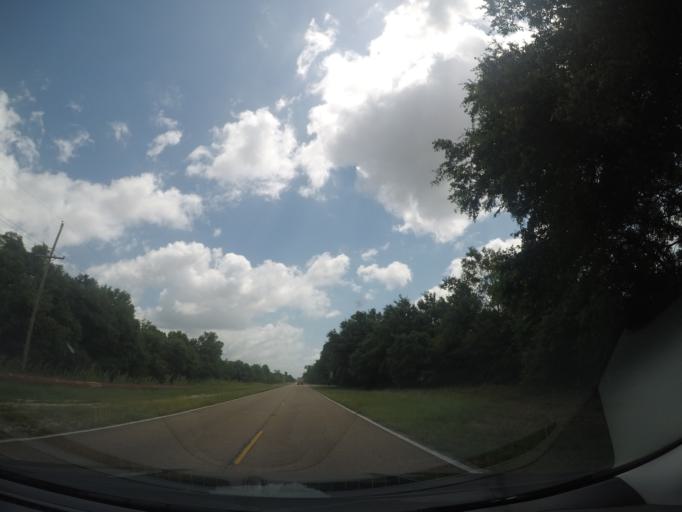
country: US
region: Louisiana
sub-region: Saint Tammany Parish
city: Eden Isle
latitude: 30.1904
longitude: -89.7141
